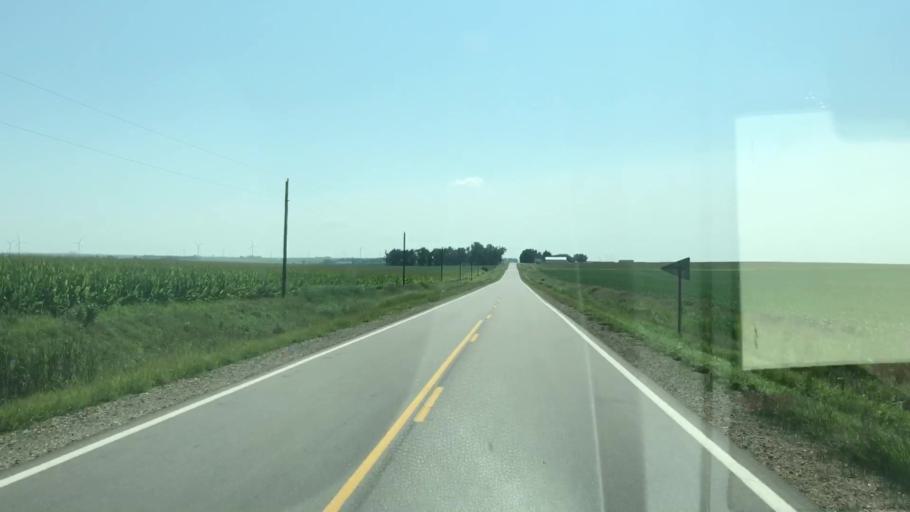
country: US
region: Iowa
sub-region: O'Brien County
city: Sanborn
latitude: 43.2700
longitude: -95.7237
